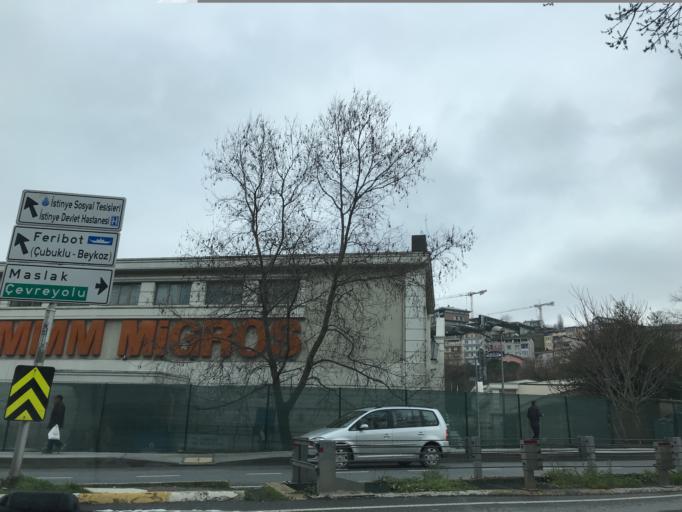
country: TR
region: Istanbul
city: Sisli
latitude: 41.1168
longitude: 29.0501
